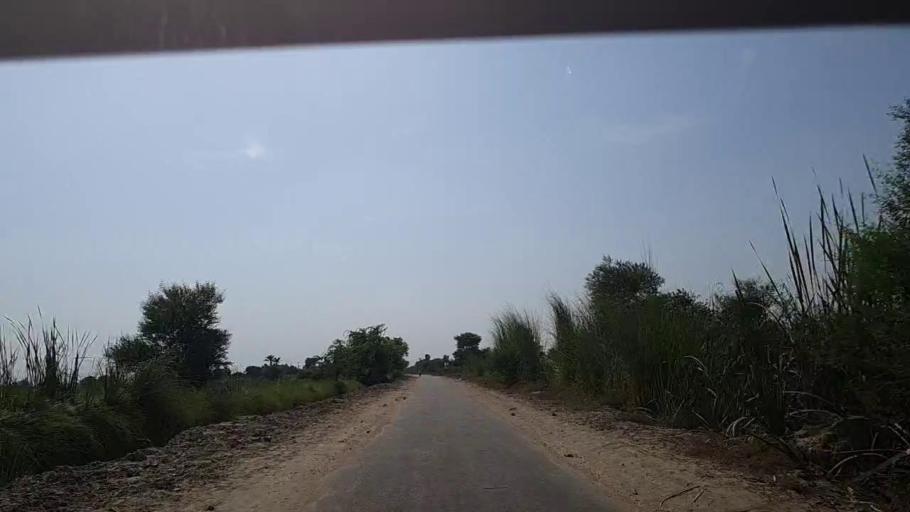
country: PK
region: Sindh
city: Khanpur
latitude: 27.8439
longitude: 69.4038
